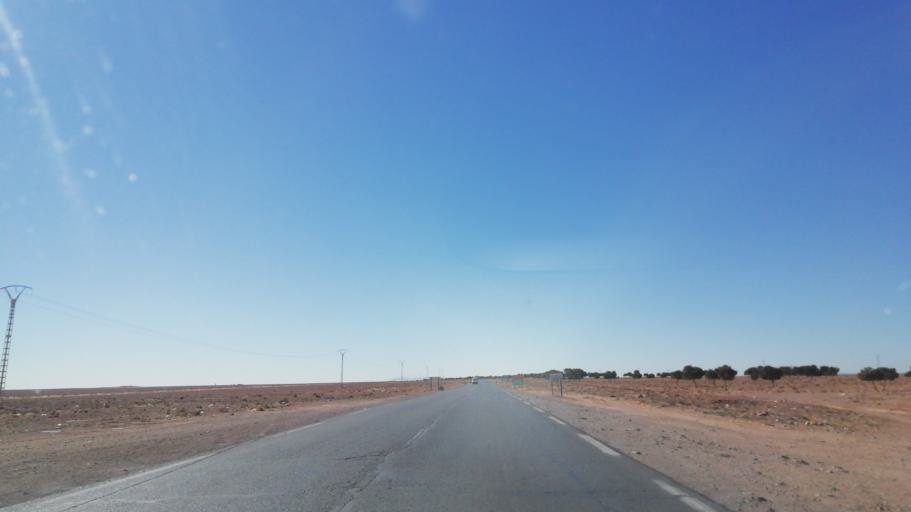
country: DZ
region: Saida
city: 'Ain el Hadjar
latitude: 34.0063
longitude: 0.0489
